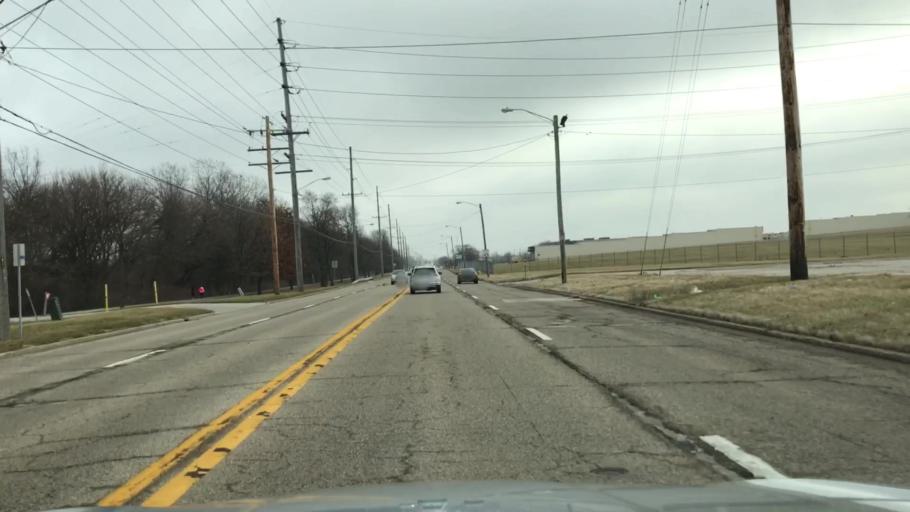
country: US
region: Illinois
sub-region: McLean County
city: Normal
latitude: 40.5027
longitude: -88.9480
